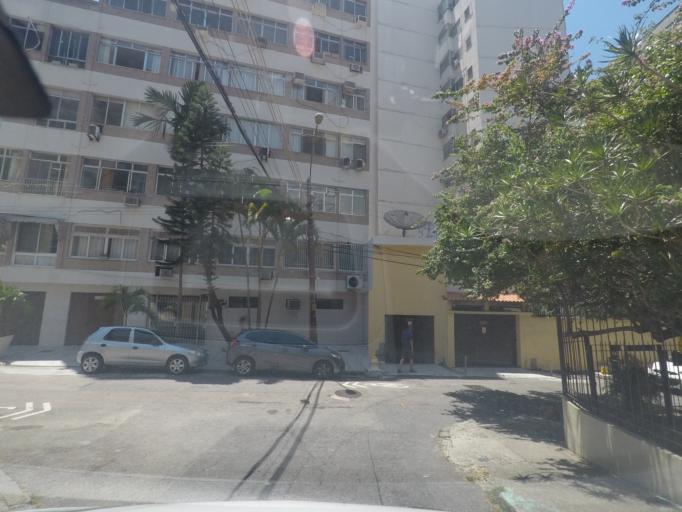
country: BR
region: Rio de Janeiro
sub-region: Rio De Janeiro
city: Rio de Janeiro
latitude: -22.9633
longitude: -43.1804
